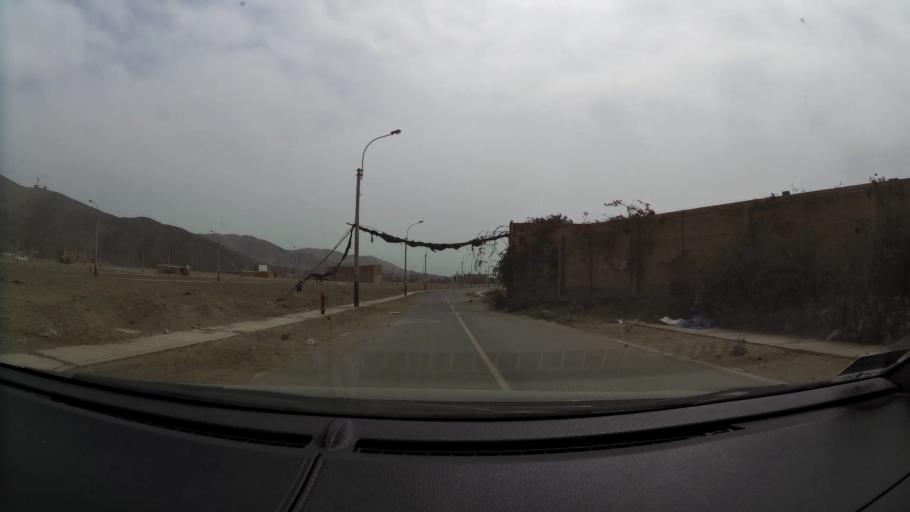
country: PE
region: Lima
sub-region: Lima
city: Santa Rosa
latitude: -11.7931
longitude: -77.1476
